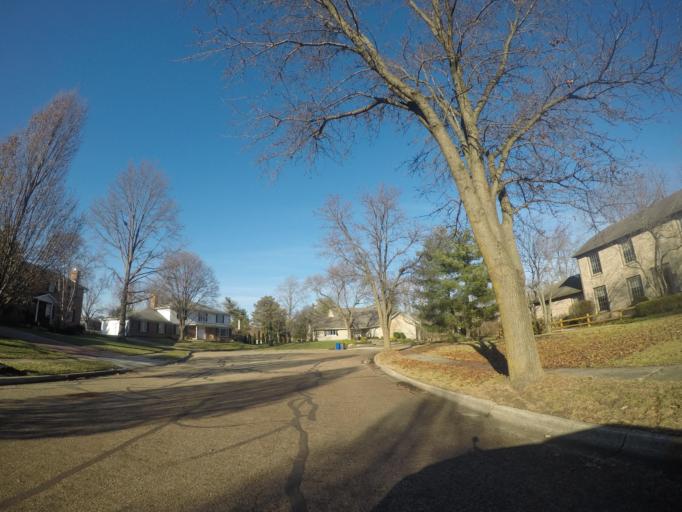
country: US
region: Ohio
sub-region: Franklin County
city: Upper Arlington
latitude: 40.0394
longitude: -83.0701
